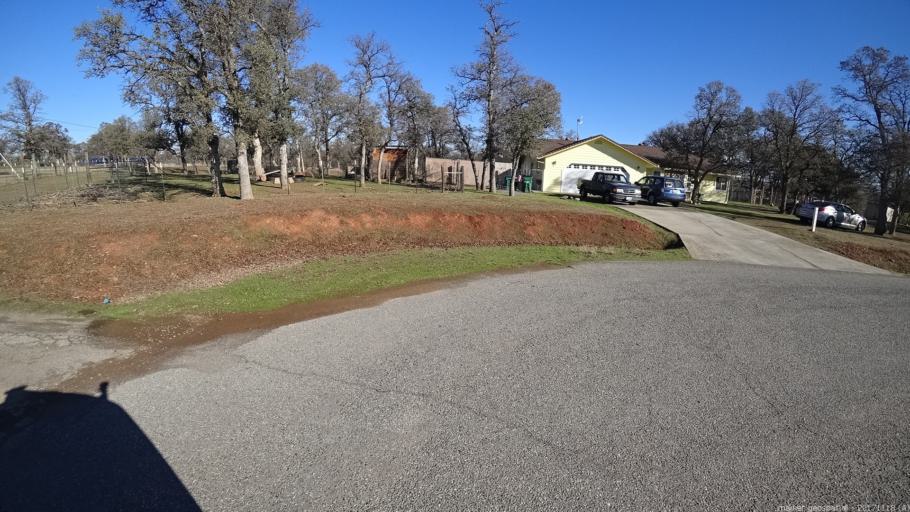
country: US
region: California
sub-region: Shasta County
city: Cottonwood
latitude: 40.3950
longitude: -122.3236
